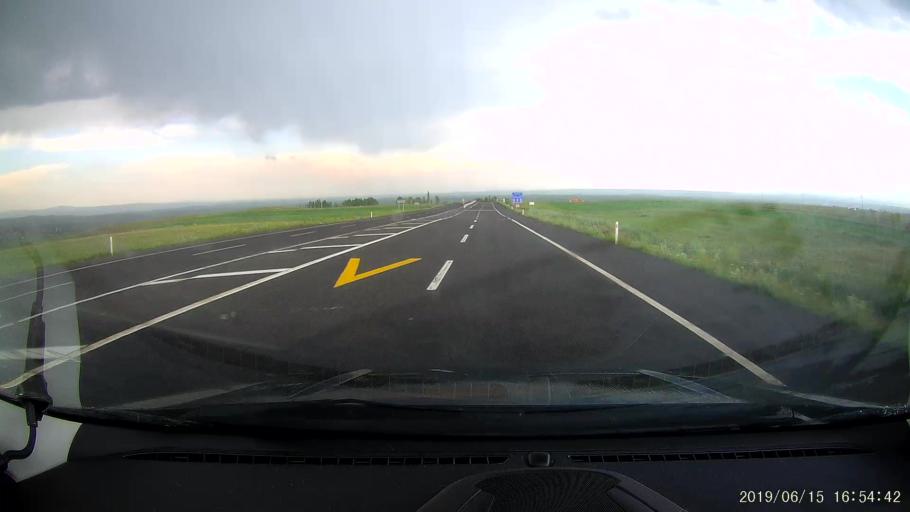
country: TR
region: Kars
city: Susuz
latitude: 40.7890
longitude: 43.1299
